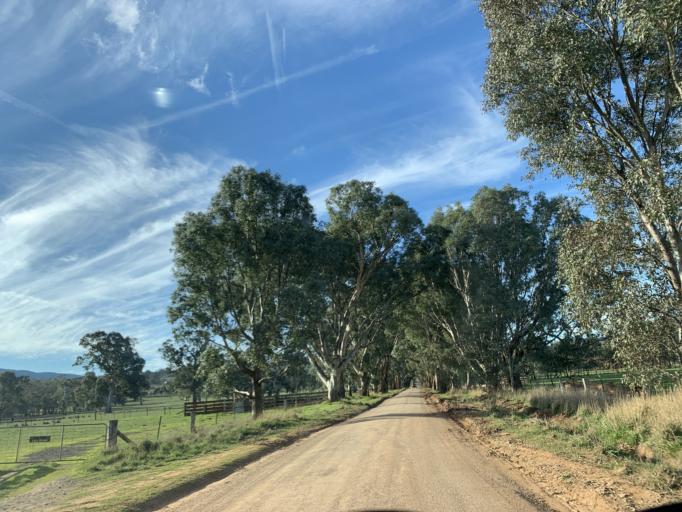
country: AU
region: Victoria
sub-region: Mansfield
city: Mansfield
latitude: -36.9665
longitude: 146.1064
